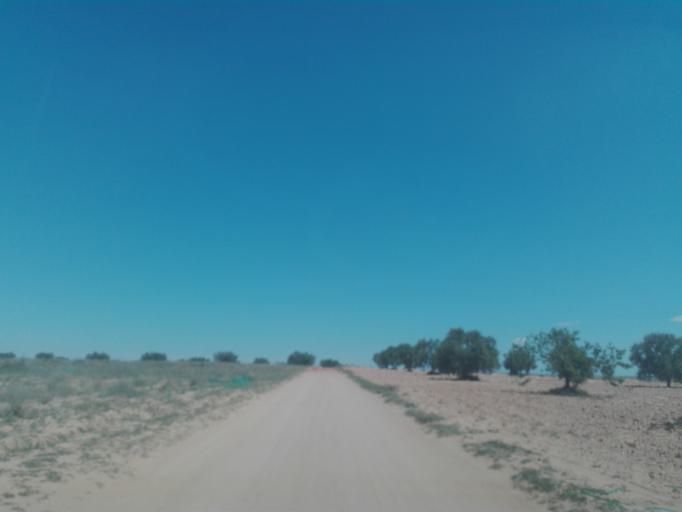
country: TN
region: Safaqis
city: Sfax
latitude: 34.7298
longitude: 10.4313
